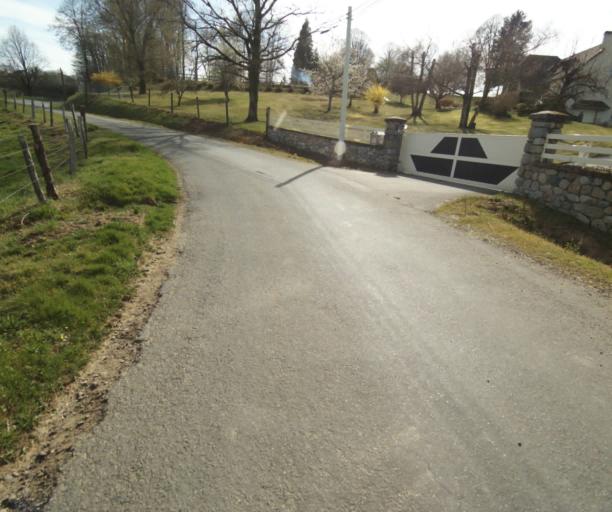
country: FR
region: Limousin
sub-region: Departement de la Correze
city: Seilhac
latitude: 45.3473
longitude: 1.7457
